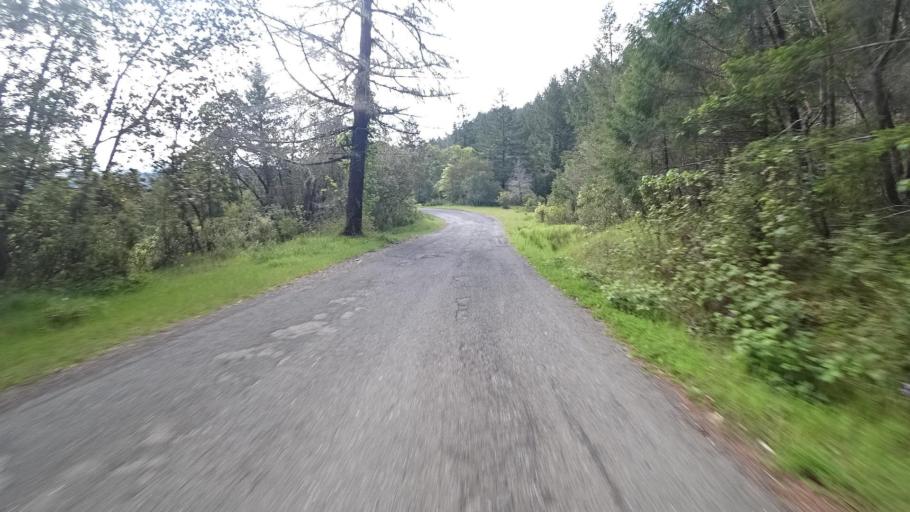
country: US
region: California
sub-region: Humboldt County
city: Redway
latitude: 40.2161
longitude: -123.6538
